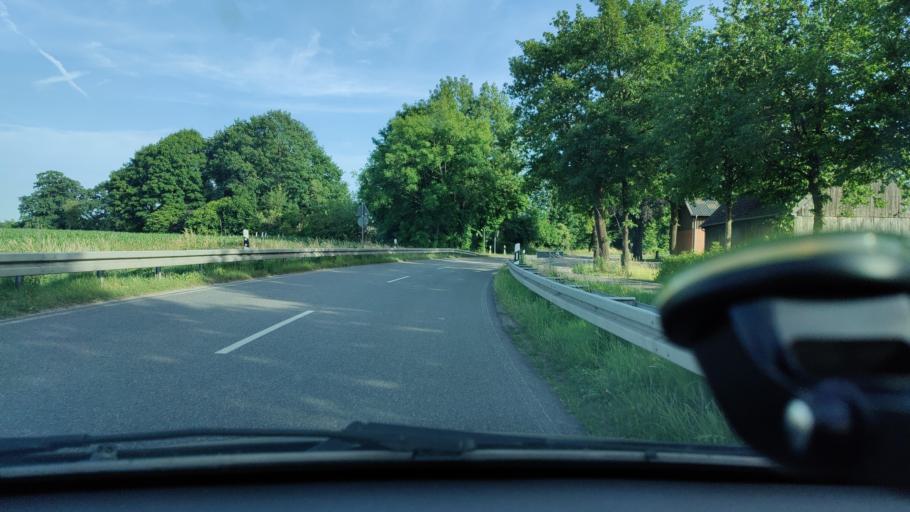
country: DE
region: North Rhine-Westphalia
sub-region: Regierungsbezirk Munster
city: Coesfeld
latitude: 52.0103
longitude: 7.1910
